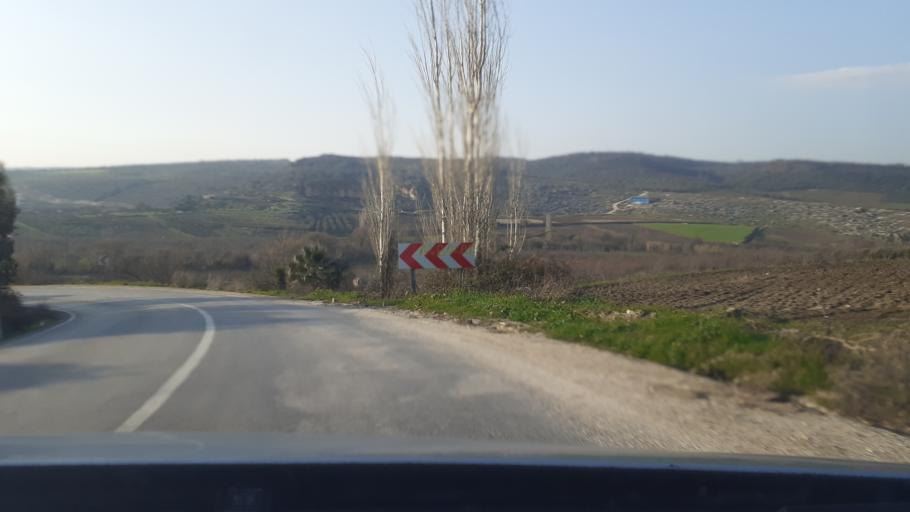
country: TR
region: Hatay
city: Oymakli
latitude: 36.1149
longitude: 36.2834
